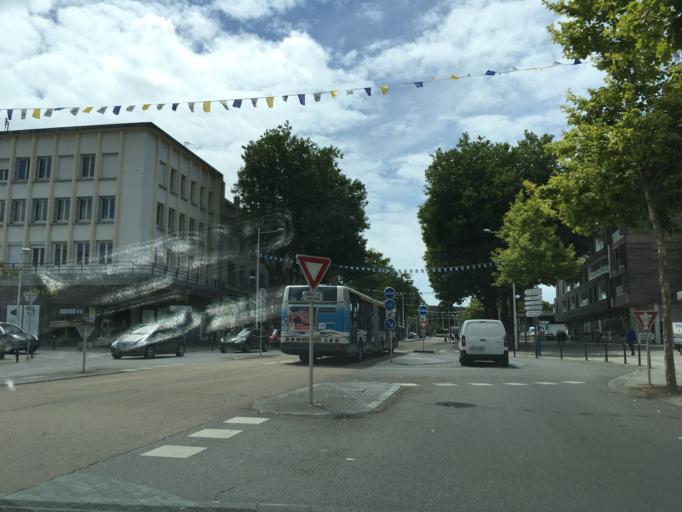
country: FR
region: Brittany
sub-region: Departement du Morbihan
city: Lorient
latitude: 47.7469
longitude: -3.3661
